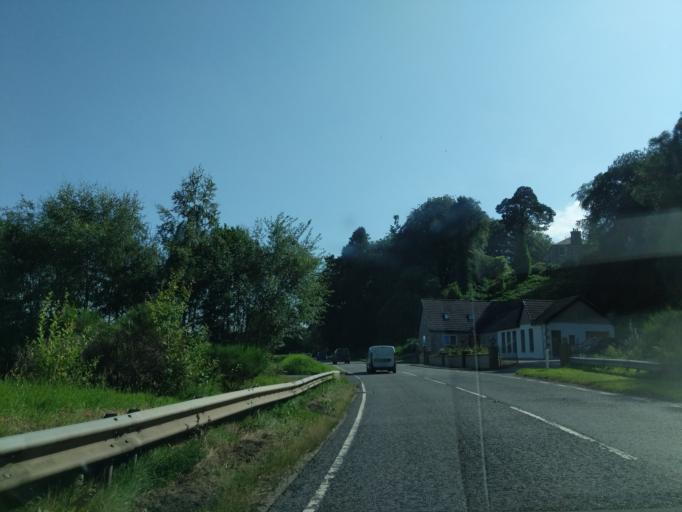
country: GB
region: Scotland
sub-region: Moray
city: Rothes
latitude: 57.5204
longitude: -3.2093
